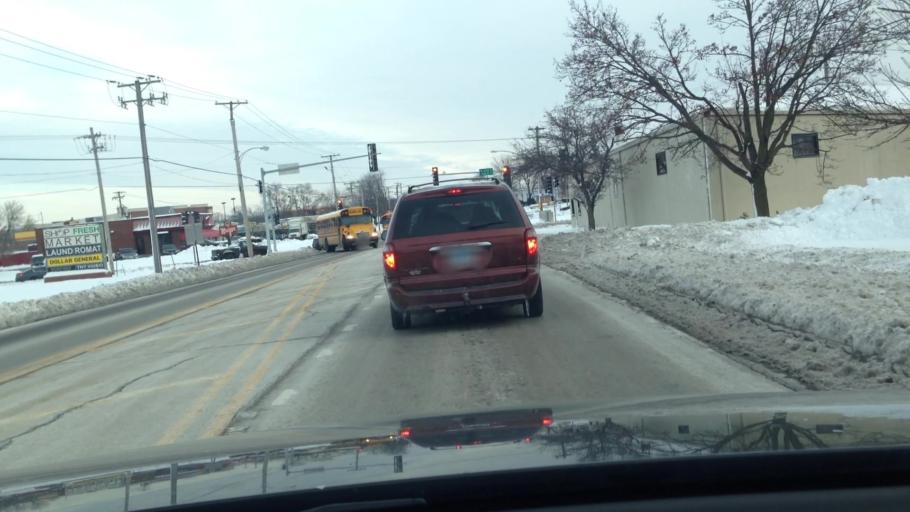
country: US
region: Illinois
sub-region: McHenry County
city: Woodstock
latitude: 42.3163
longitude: -88.4392
